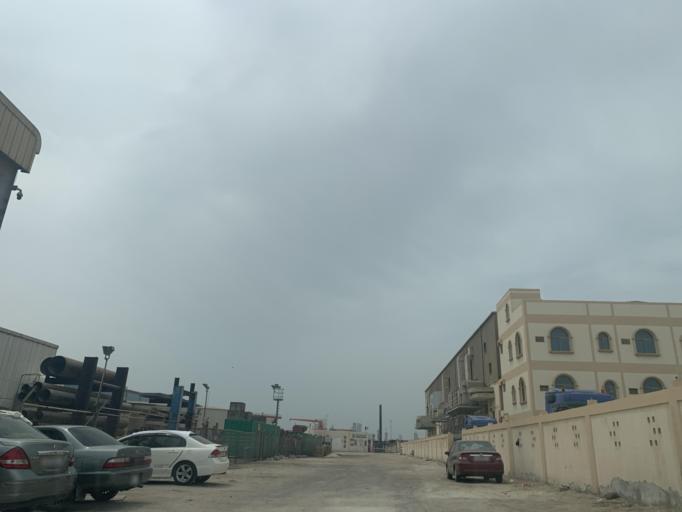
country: BH
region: Muharraq
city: Al Hadd
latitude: 26.2162
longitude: 50.6538
